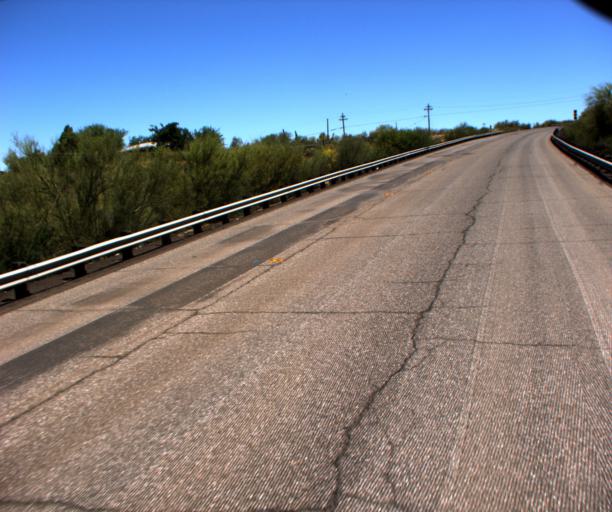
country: US
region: Arizona
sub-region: Pinal County
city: Mammoth
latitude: 32.6984
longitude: -110.6441
